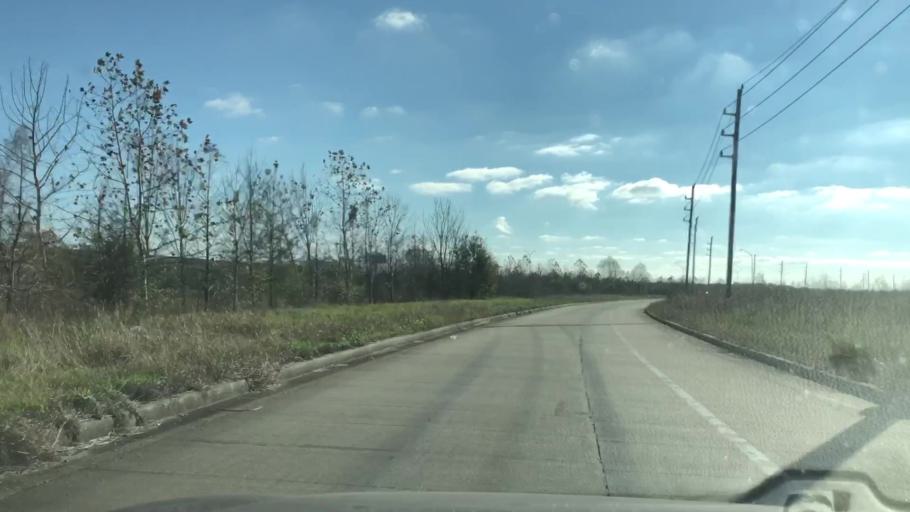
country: US
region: Texas
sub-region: Harris County
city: Cloverleaf
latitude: 29.8296
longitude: -95.1755
